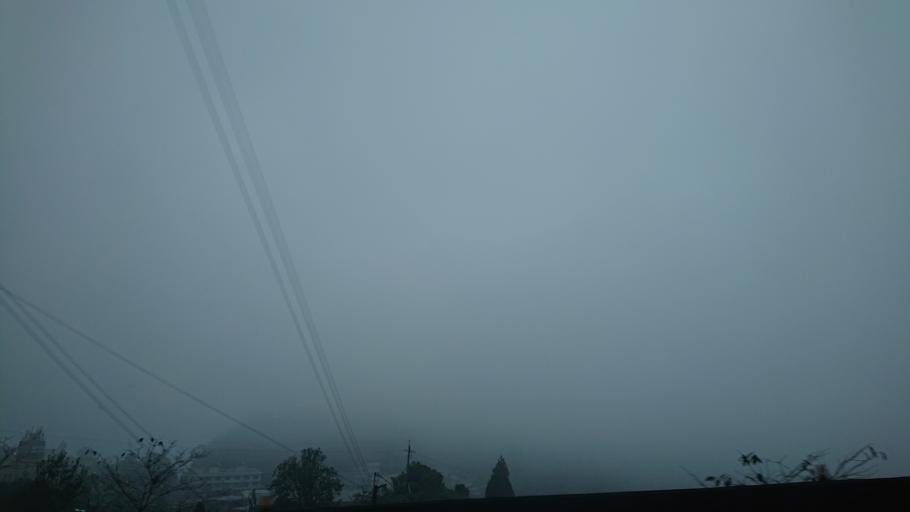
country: TW
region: Taiwan
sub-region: Chiayi
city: Jiayi Shi
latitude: 23.4760
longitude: 120.6963
